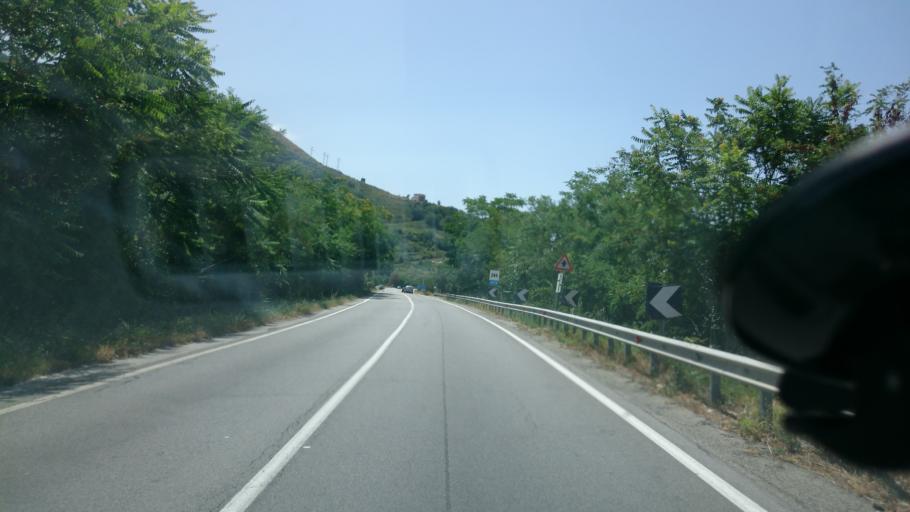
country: IT
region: Calabria
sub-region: Provincia di Cosenza
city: Cittadella del Capo
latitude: 39.5902
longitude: 15.8685
